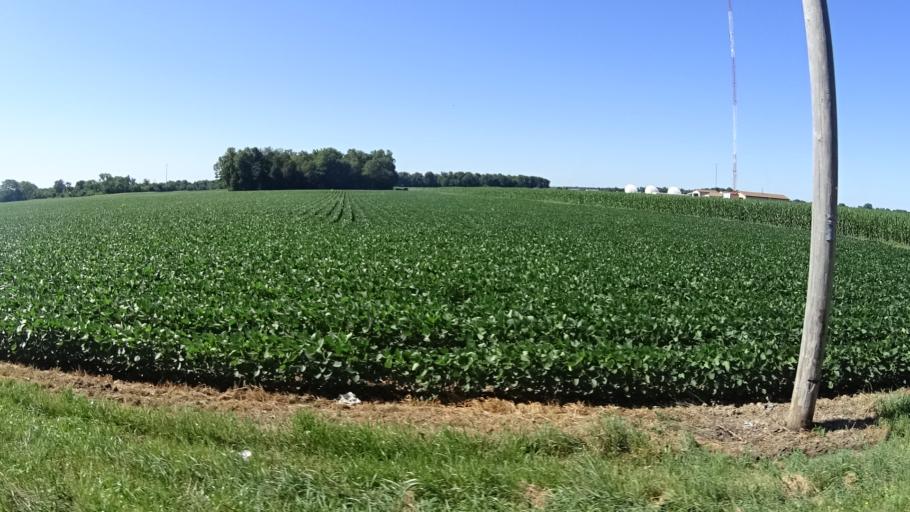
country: US
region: Ohio
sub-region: Erie County
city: Sandusky
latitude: 41.4088
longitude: -82.7129
